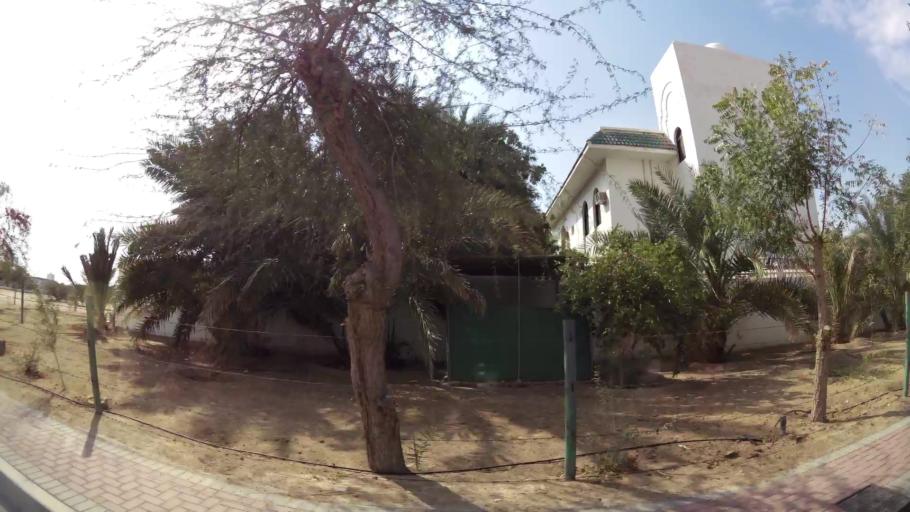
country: AE
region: Abu Dhabi
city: Al Ain
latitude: 24.0980
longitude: 55.9075
